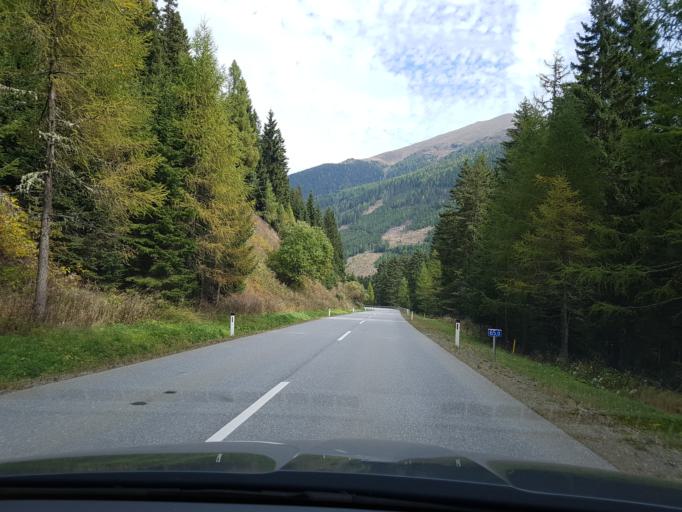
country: AT
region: Salzburg
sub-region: Politischer Bezirk Tamsweg
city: Ramingstein
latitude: 46.9381
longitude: 13.8813
